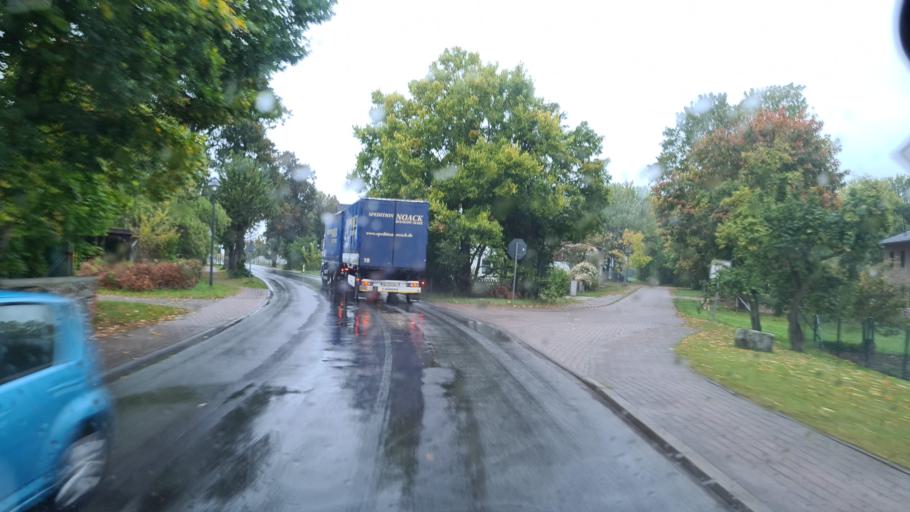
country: DE
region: Brandenburg
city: Rietz Neuendorf
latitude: 52.2681
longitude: 14.1634
